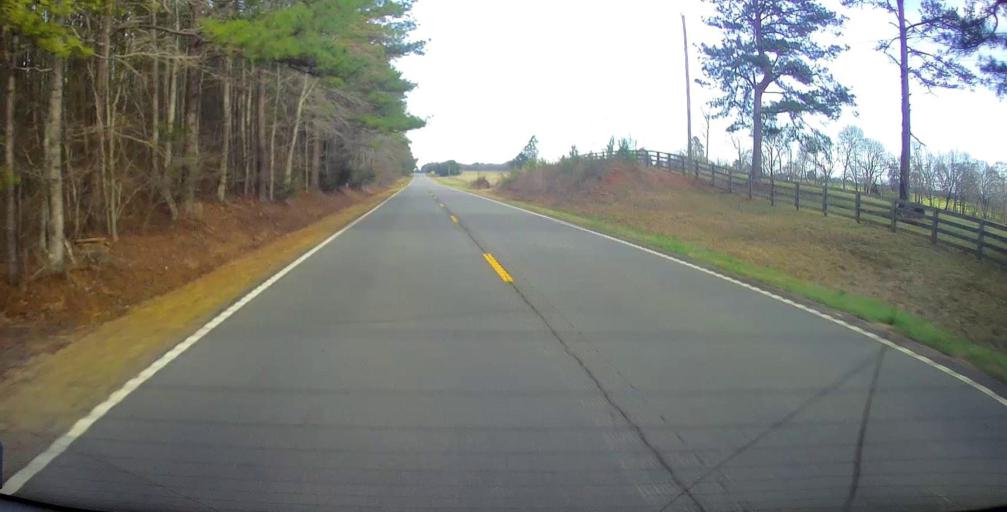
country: US
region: Georgia
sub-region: Harris County
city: Hamilton
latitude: 32.6848
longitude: -84.7629
